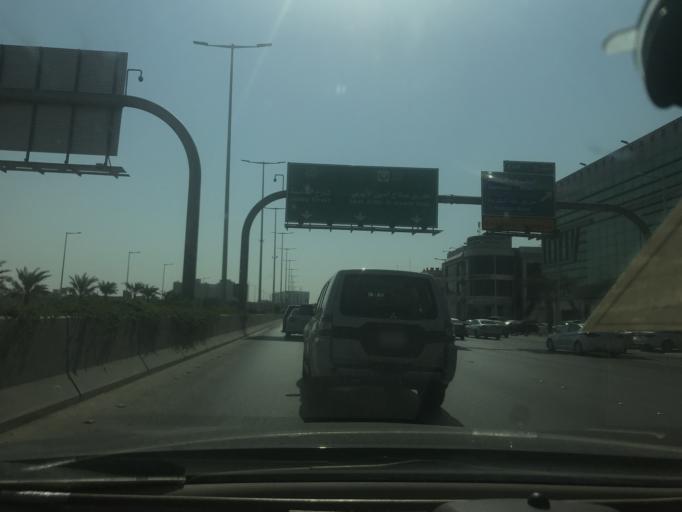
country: SA
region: Ar Riyad
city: Riyadh
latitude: 24.6983
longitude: 46.7230
